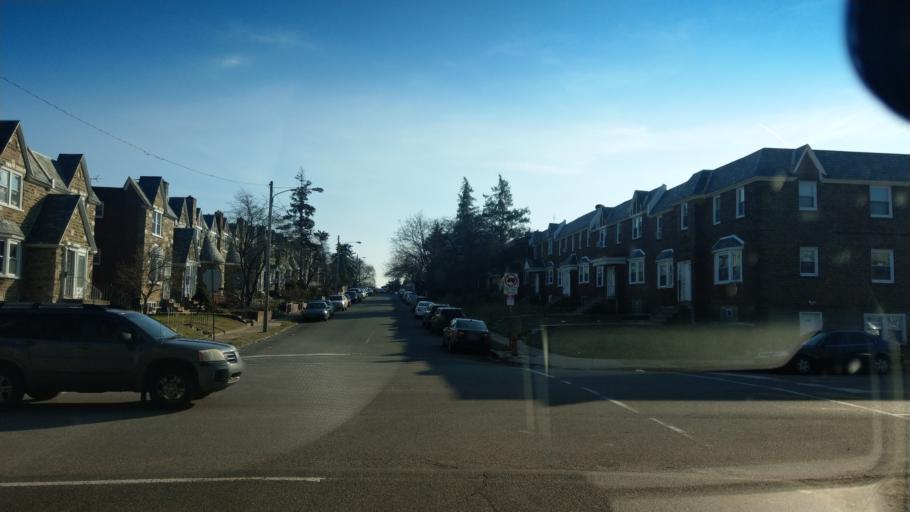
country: US
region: Pennsylvania
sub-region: Montgomery County
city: Rockledge
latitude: 40.0292
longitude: -75.1152
